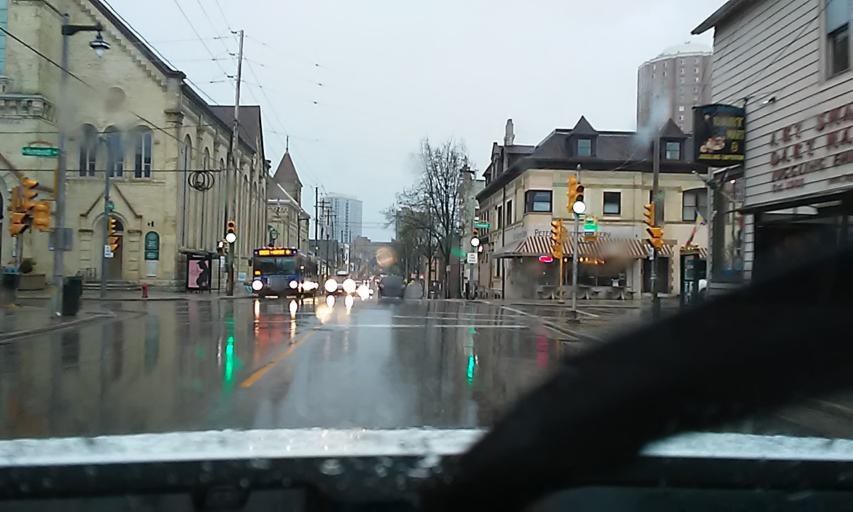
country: US
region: Wisconsin
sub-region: Milwaukee County
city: Milwaukee
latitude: 43.0530
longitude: -87.8985
